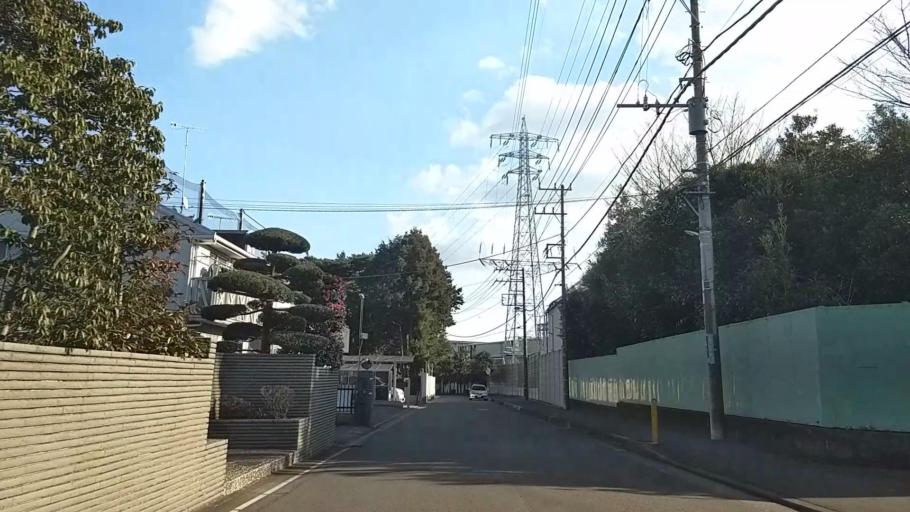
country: JP
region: Kanagawa
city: Atsugi
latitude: 35.4533
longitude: 139.3352
